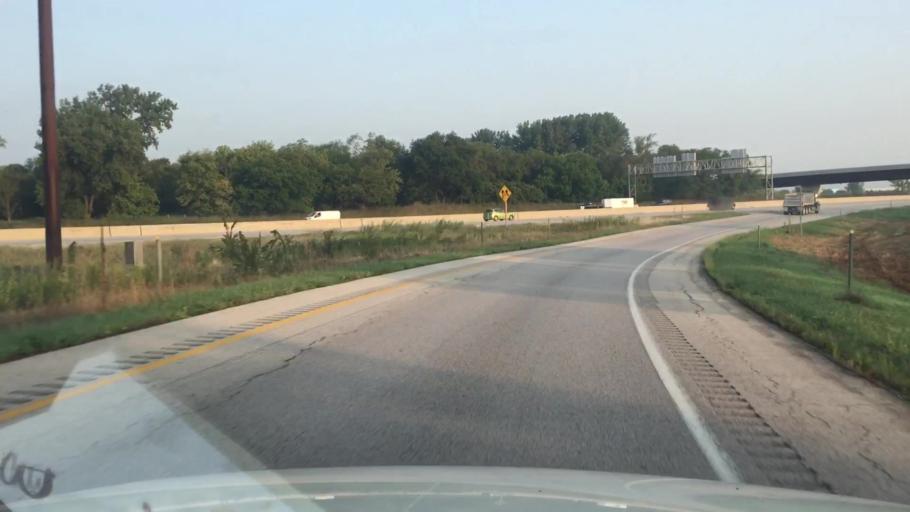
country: US
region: Iowa
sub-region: Polk County
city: Saylorville
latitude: 41.6562
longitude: -93.5748
